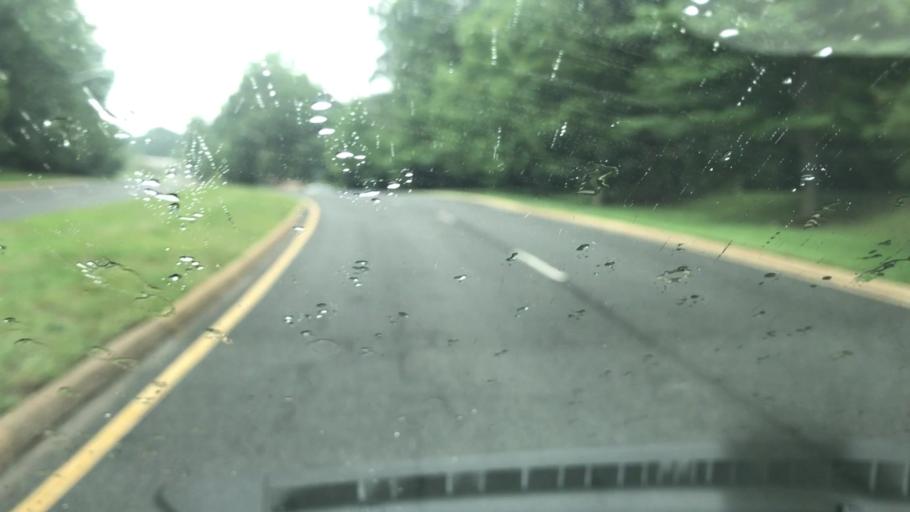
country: US
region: Virginia
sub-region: Fairfax County
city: Greenbriar
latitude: 38.8670
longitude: -77.3745
